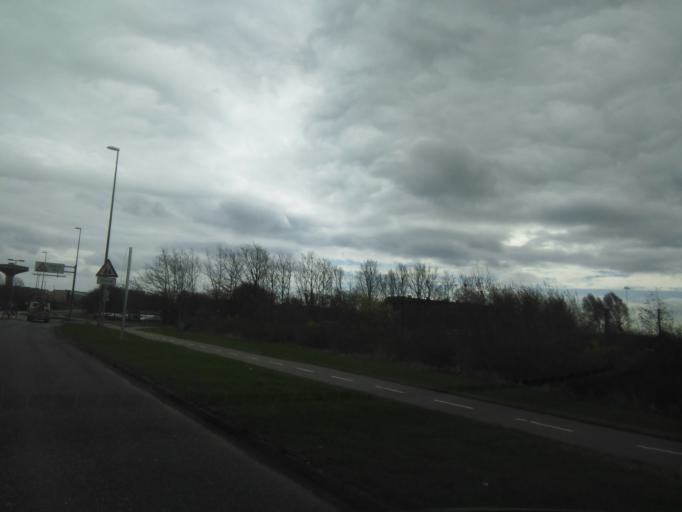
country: DK
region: Central Jutland
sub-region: Arhus Kommune
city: Stavtrup
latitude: 56.1713
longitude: 10.1474
